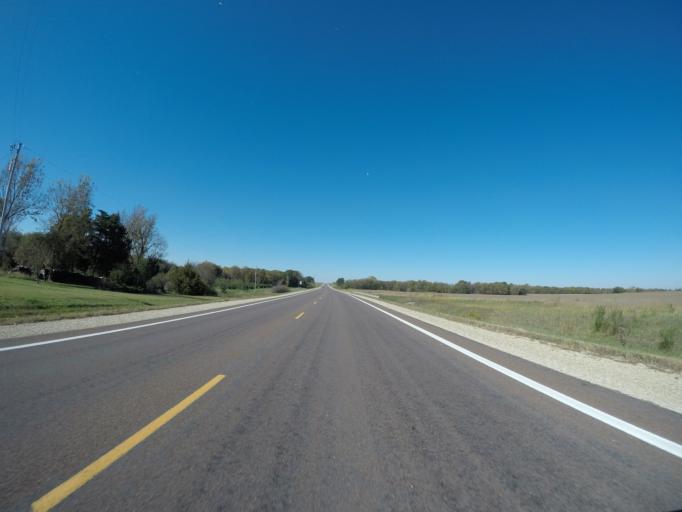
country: US
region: Kansas
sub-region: Riley County
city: Fort Riley North
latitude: 39.3060
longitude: -96.8503
